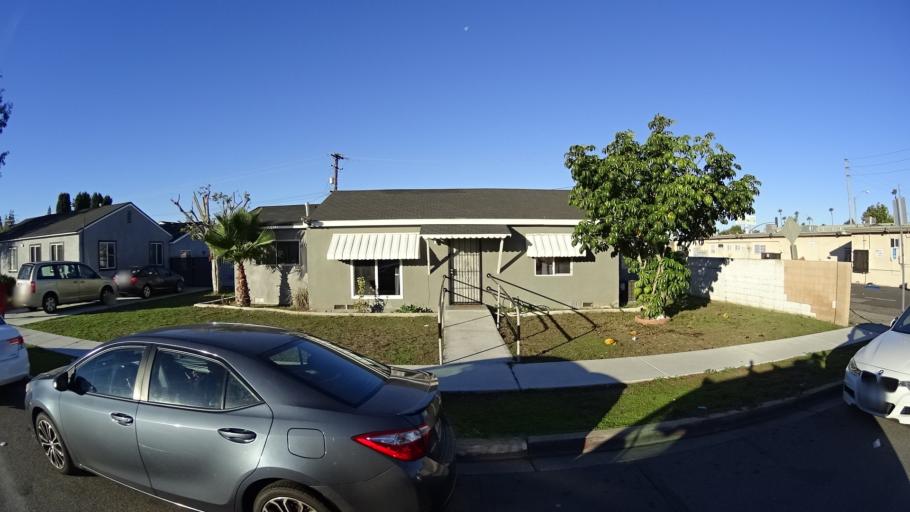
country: US
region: California
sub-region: Orange County
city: Westminster
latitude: 33.7733
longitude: -117.9834
